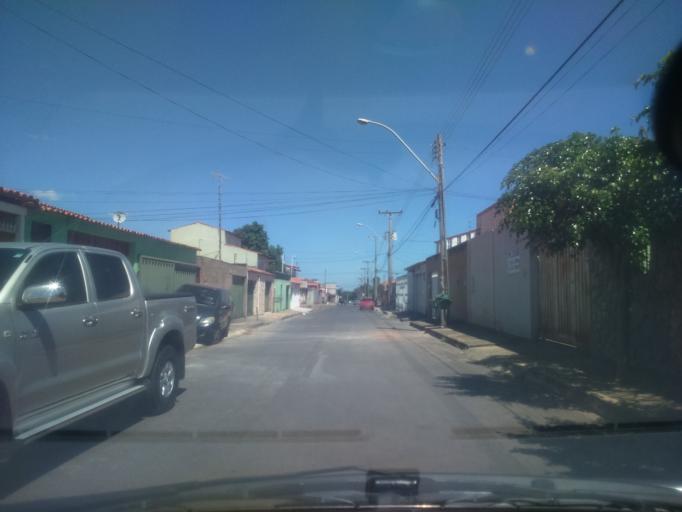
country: BR
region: Goias
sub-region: Luziania
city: Luziania
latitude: -16.0124
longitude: -48.0519
